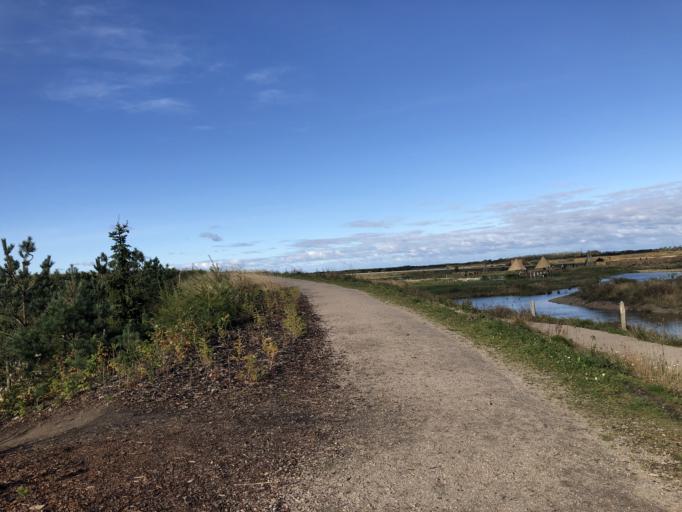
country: DK
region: Central Jutland
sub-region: Ringkobing-Skjern Kommune
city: Ringkobing
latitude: 56.1019
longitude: 8.2423
